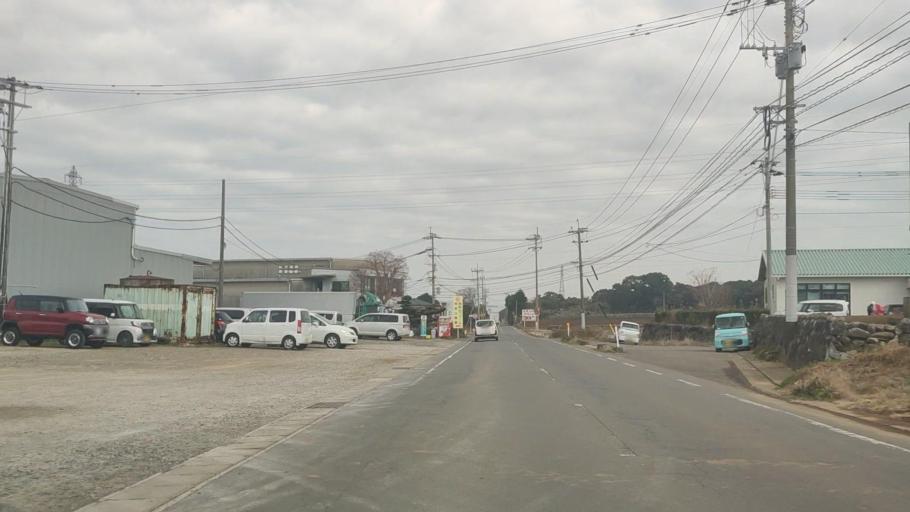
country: JP
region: Nagasaki
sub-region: Isahaya-shi
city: Isahaya
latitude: 32.8035
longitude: 130.1670
